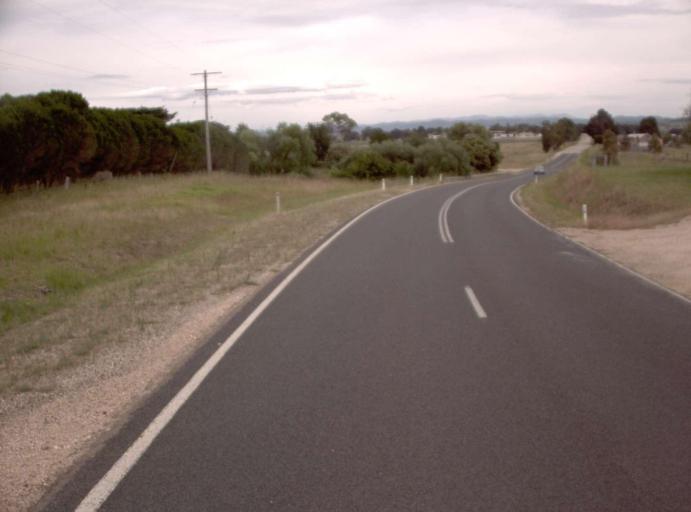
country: AU
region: Victoria
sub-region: East Gippsland
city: Bairnsdale
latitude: -37.8180
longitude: 147.4944
